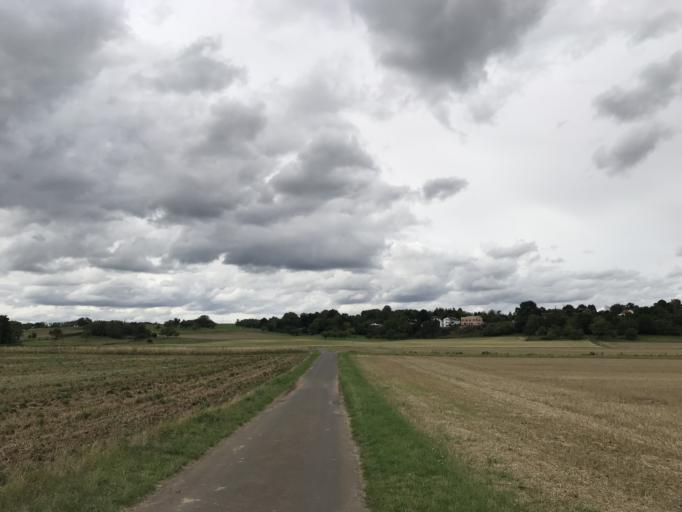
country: DE
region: Hesse
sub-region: Regierungsbezirk Giessen
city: Grunberg
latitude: 50.5595
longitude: 8.9152
